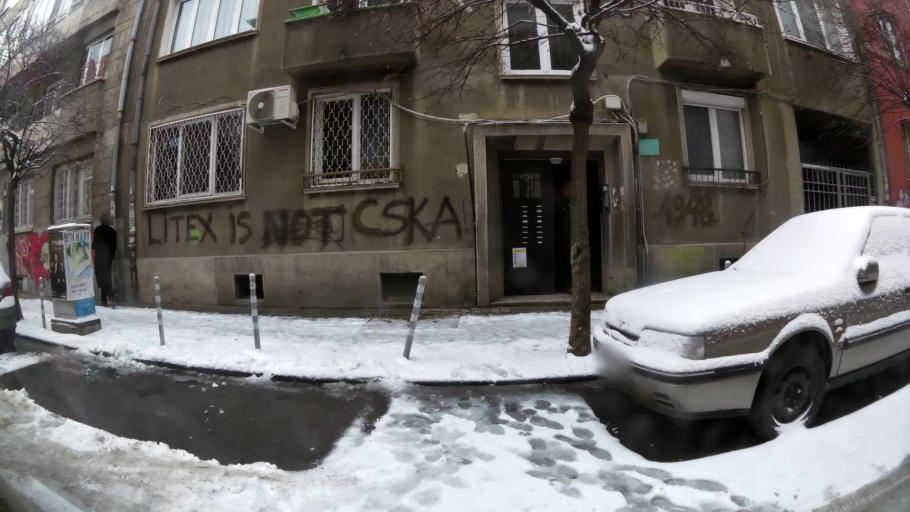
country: BG
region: Sofia-Capital
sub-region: Stolichna Obshtina
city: Sofia
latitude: 42.6912
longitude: 23.3148
